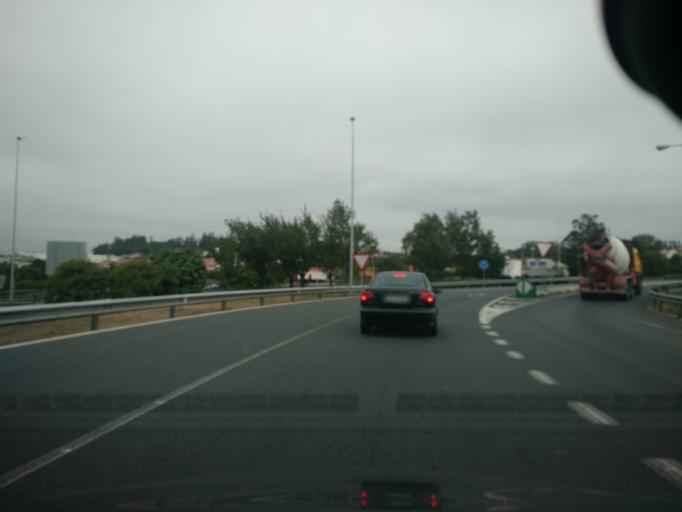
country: ES
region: Galicia
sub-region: Provincia da Coruna
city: Santiago de Compostela
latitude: 42.8896
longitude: -8.5080
